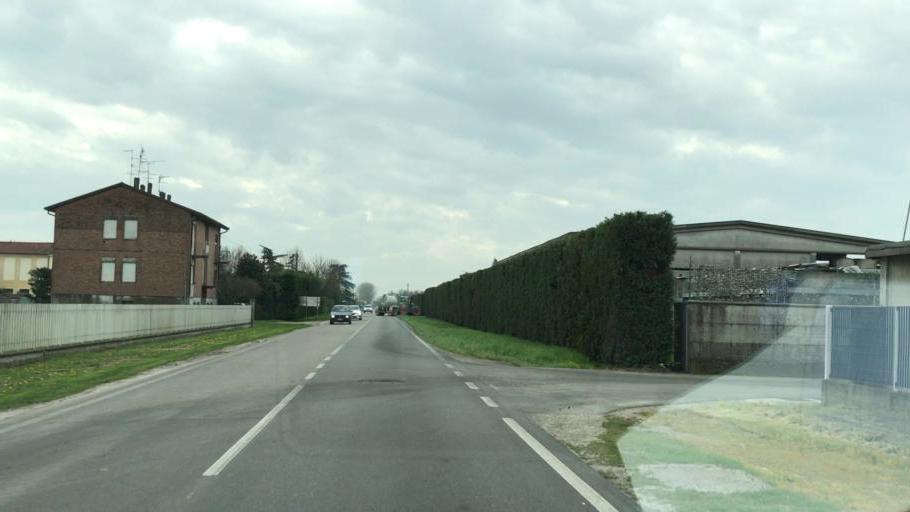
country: IT
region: Lombardy
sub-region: Provincia di Mantova
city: Commessaggio
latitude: 44.9909
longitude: 10.5768
